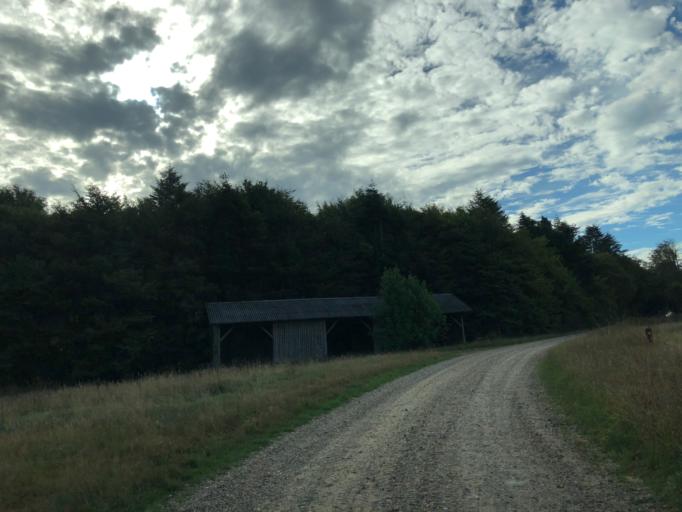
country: DK
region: Central Jutland
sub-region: Holstebro Kommune
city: Ulfborg
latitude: 56.1629
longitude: 8.4054
